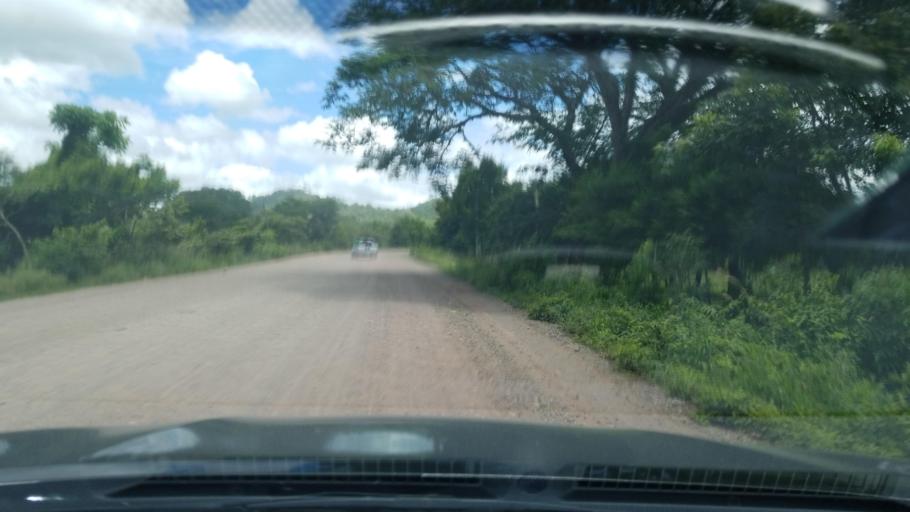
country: HN
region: Francisco Morazan
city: Talanga
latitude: 14.3731
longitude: -87.0606
